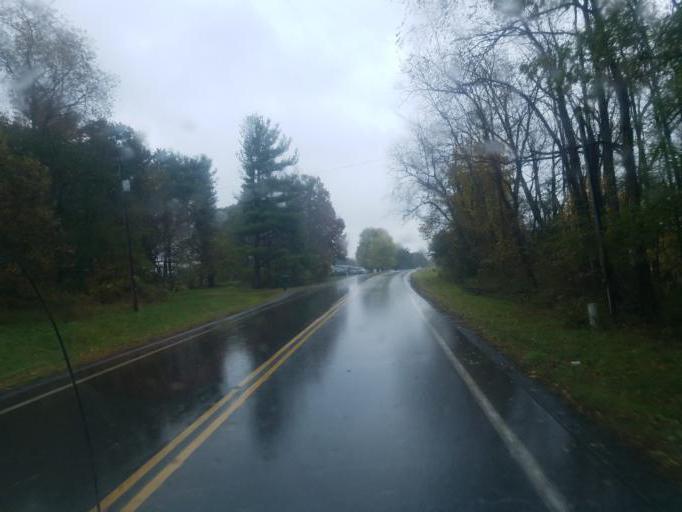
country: US
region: Ohio
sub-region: Licking County
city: Utica
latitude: 40.2548
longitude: -82.3328
